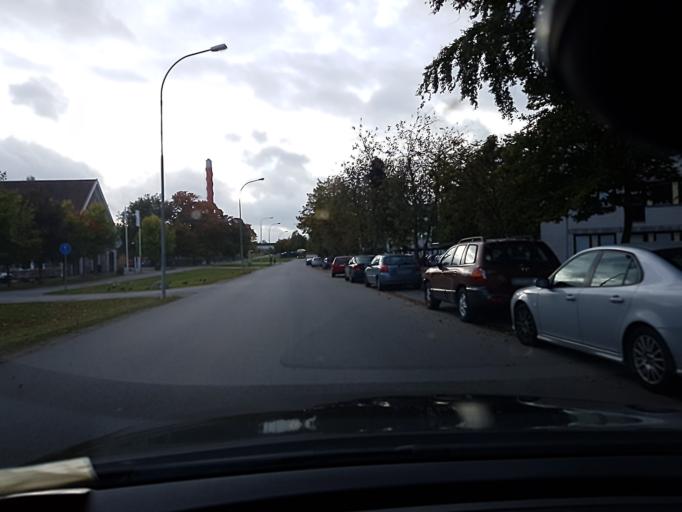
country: SE
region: Kronoberg
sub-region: Vaxjo Kommun
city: Vaexjoe
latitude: 56.8512
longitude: 14.8279
